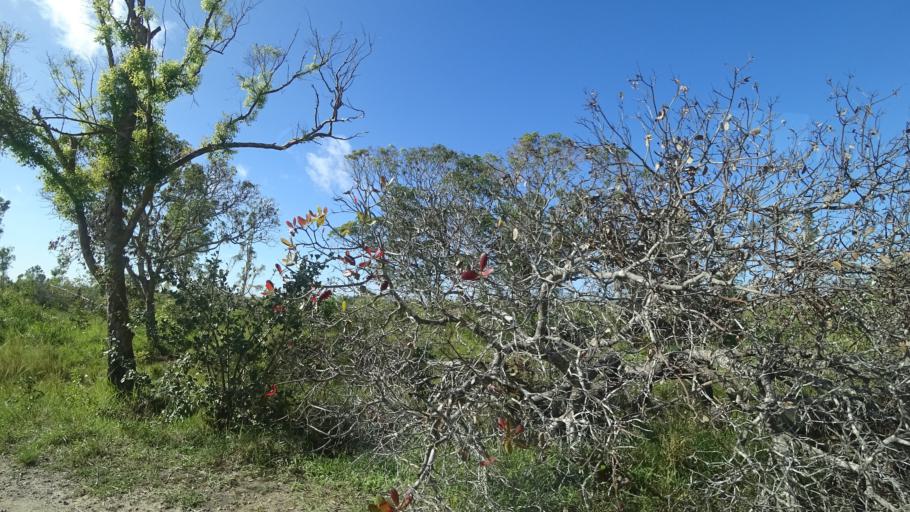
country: MZ
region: Sofala
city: Beira
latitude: -19.6912
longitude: 35.0409
